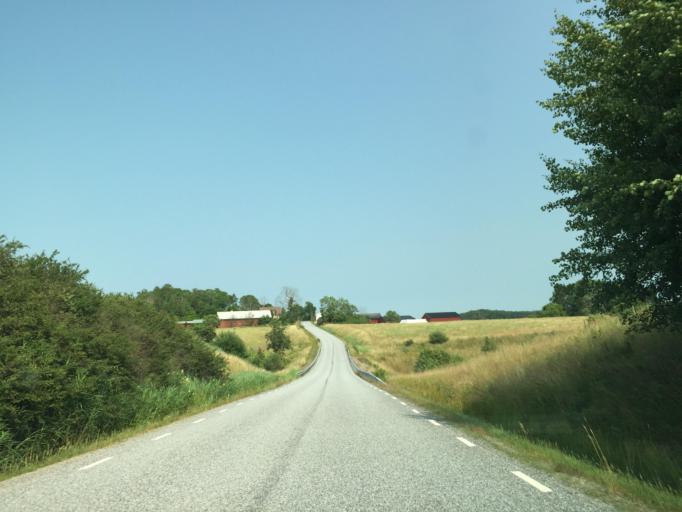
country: SE
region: Vaestra Goetaland
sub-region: Lilla Edets Kommun
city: Lilla Edet
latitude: 58.2085
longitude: 12.1310
